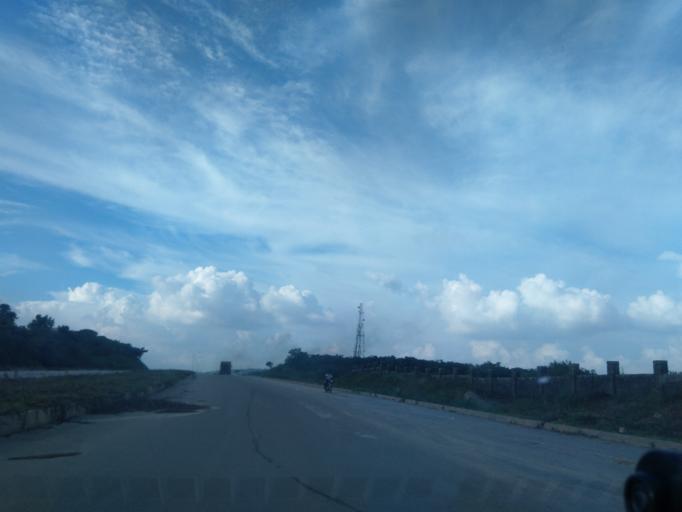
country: NG
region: Abuja Federal Capital Territory
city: Abuja
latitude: 9.0407
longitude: 7.3880
